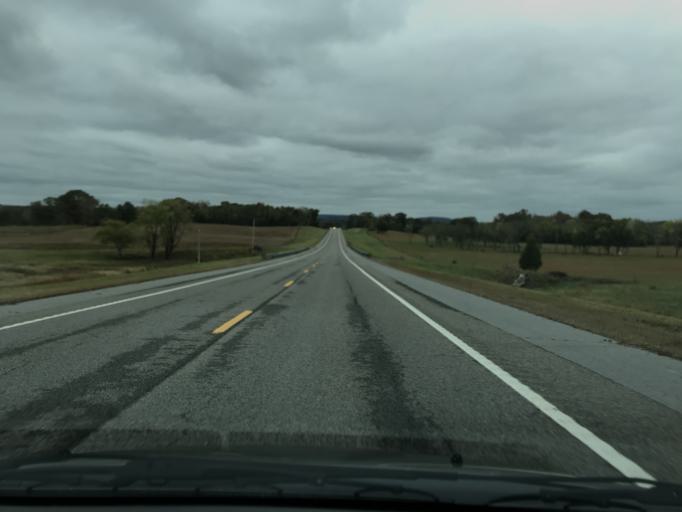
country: US
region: Tennessee
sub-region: Rhea County
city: Graysville
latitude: 35.4002
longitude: -85.0130
